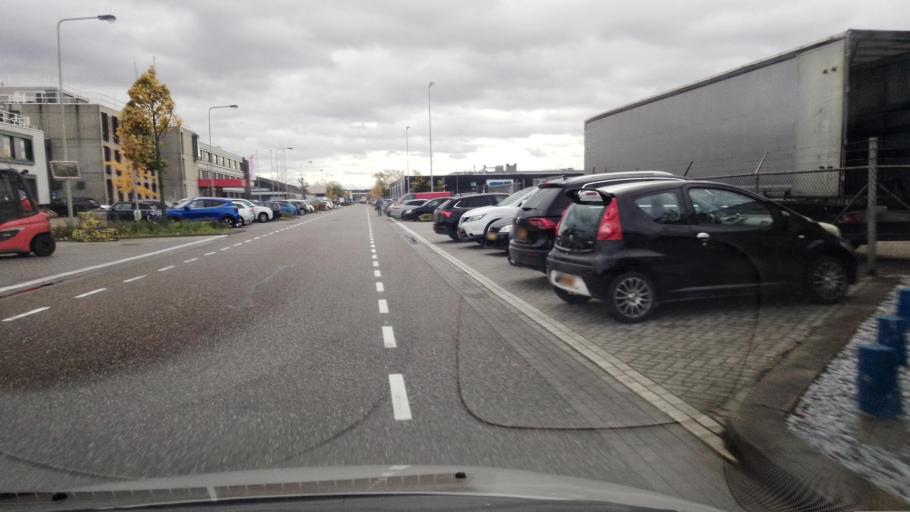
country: NL
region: Limburg
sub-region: Gemeente Roerdalen
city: Melick
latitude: 51.1704
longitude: 6.0416
